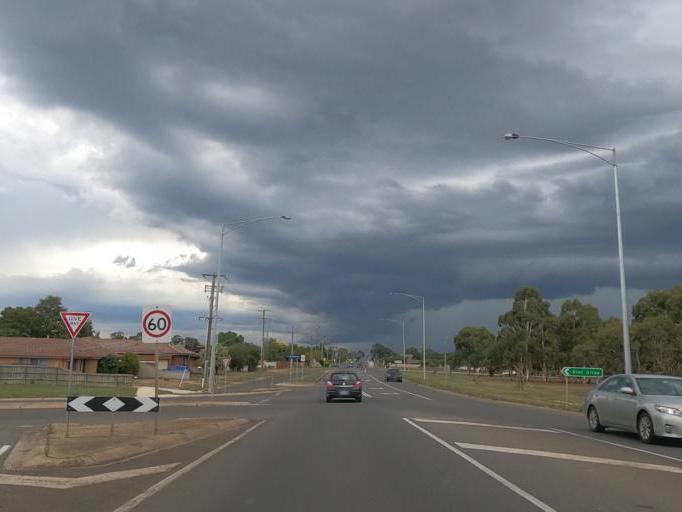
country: AU
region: Victoria
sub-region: Ballarat North
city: Lake Wendouree
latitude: -37.5193
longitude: 143.8260
